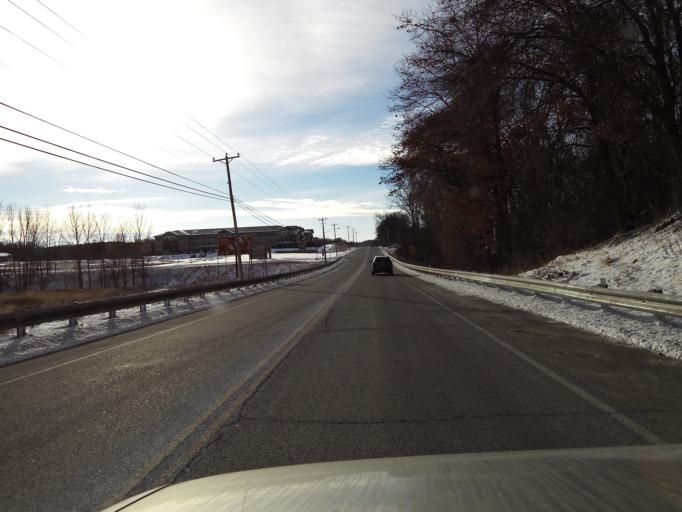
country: US
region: Minnesota
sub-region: Dakota County
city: Inver Grove Heights
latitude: 44.8470
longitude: -93.0854
